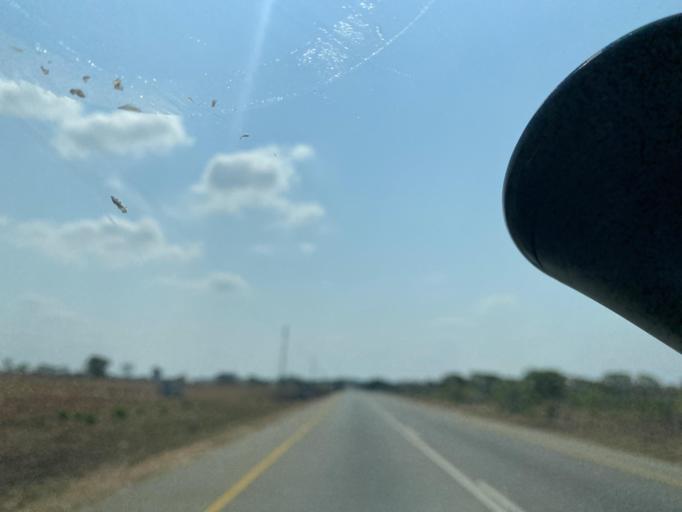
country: ZM
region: Lusaka
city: Chongwe
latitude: -15.5291
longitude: 28.6150
